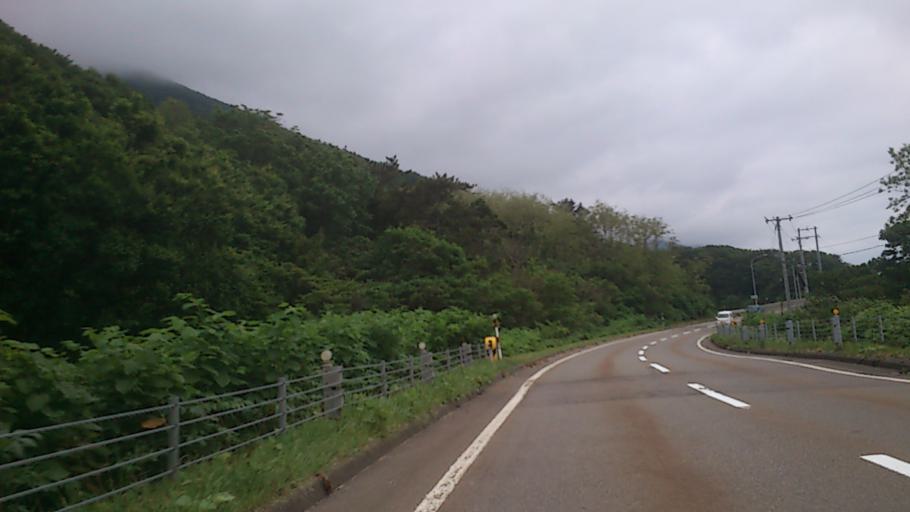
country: JP
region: Hokkaido
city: Kamiiso
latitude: 41.6746
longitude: 140.0075
